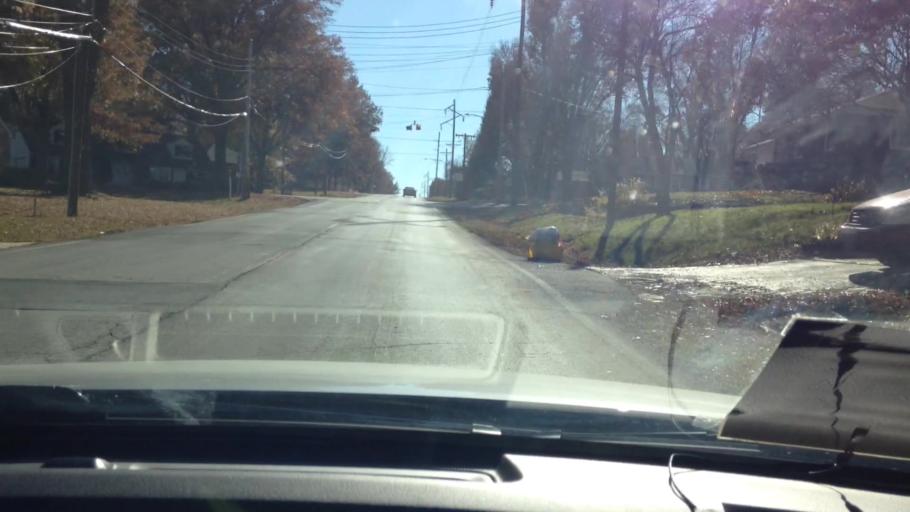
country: US
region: Missouri
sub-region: Jackson County
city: Raytown
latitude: 39.0269
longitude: -94.4485
